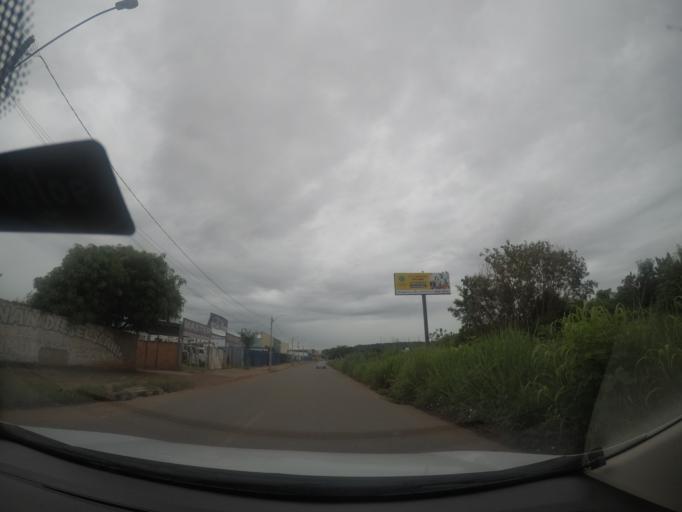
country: BR
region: Goias
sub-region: Goiania
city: Goiania
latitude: -16.6927
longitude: -49.3318
